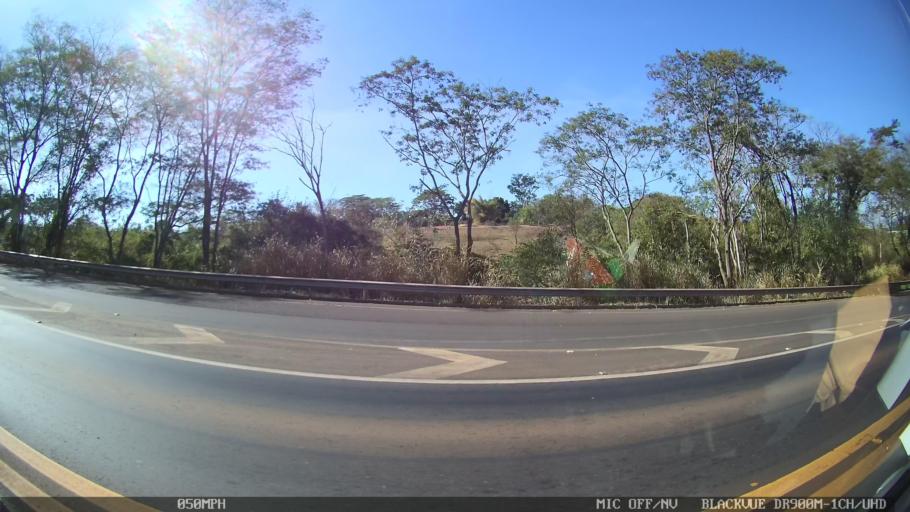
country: BR
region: Sao Paulo
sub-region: Olimpia
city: Olimpia
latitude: -20.6876
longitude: -48.9019
